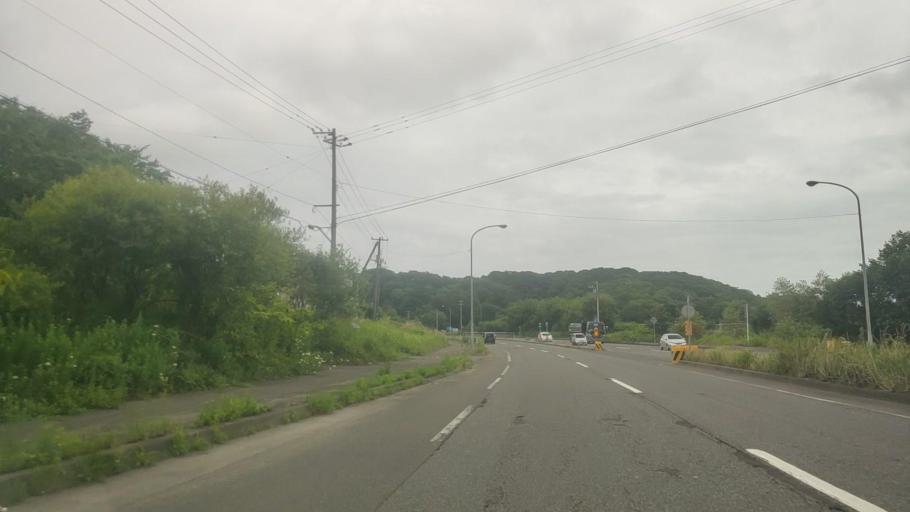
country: JP
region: Hokkaido
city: Shiraoi
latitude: 42.4565
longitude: 141.1880
